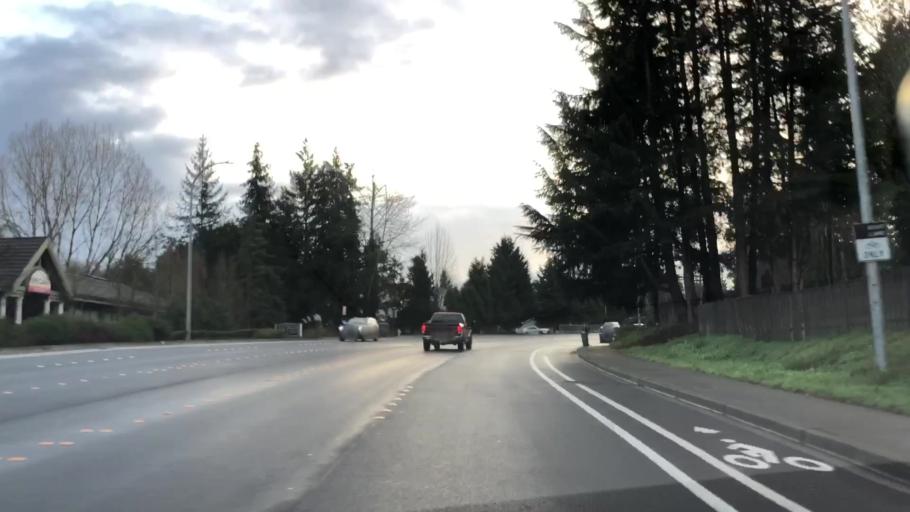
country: US
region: Washington
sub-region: King County
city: Newport
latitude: 47.5942
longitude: -122.1656
